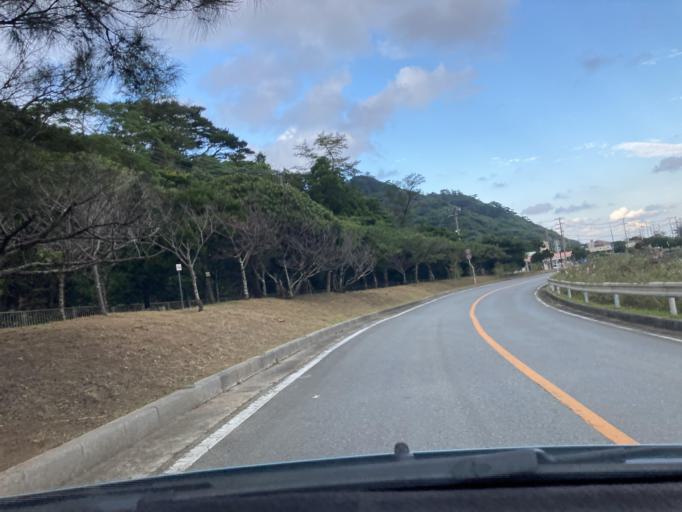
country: JP
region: Okinawa
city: Nago
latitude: 26.8358
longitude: 128.2865
